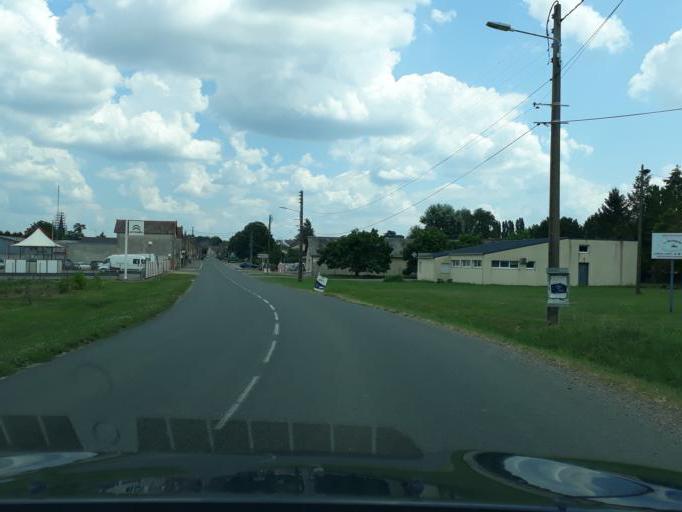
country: FR
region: Centre
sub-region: Departement du Cher
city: Nerondes
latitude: 46.9975
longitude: 2.8094
